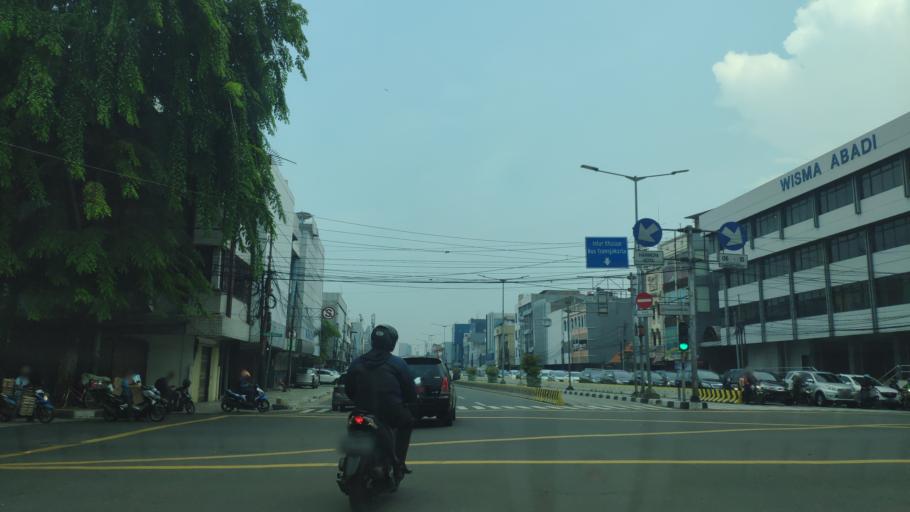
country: ID
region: Jakarta Raya
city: Jakarta
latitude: -6.1710
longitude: 106.8110
